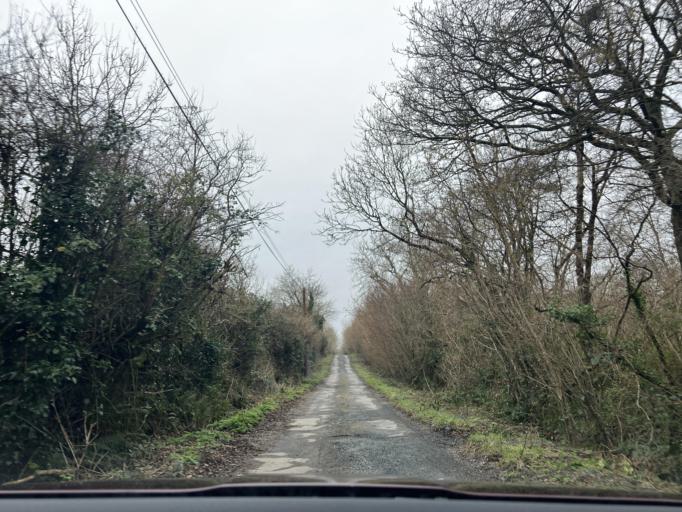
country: IE
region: Leinster
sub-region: Loch Garman
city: Castlebridge
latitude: 52.3823
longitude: -6.5504
